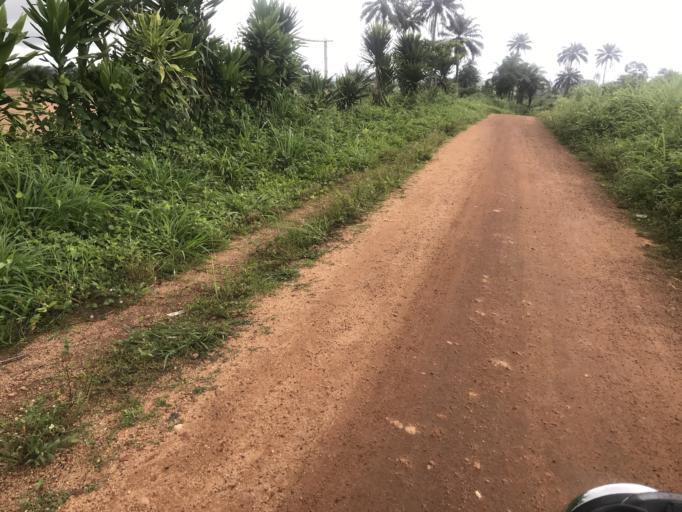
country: GN
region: Nzerekore
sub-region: Prefecture de Guekedou
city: Gueckedou
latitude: 8.4769
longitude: -10.2971
